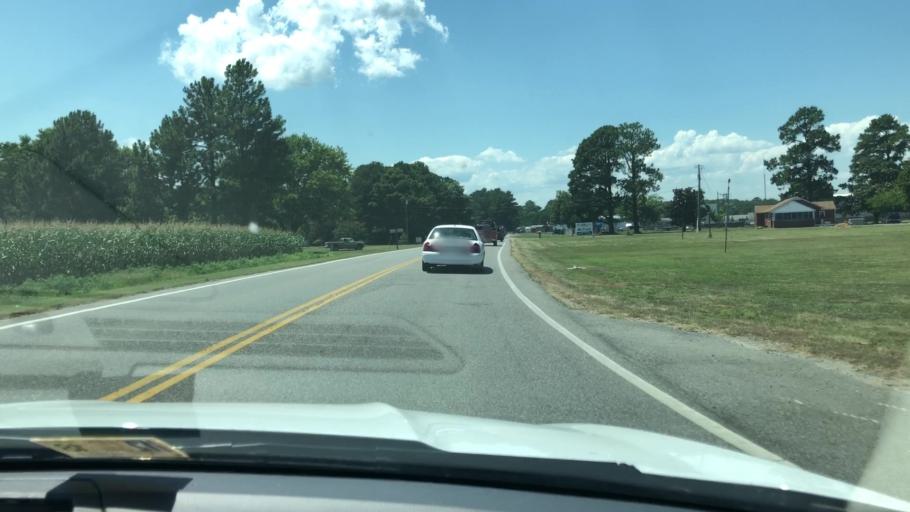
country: US
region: Virginia
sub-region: Middlesex County
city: Deltaville
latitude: 37.5984
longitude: -76.4461
